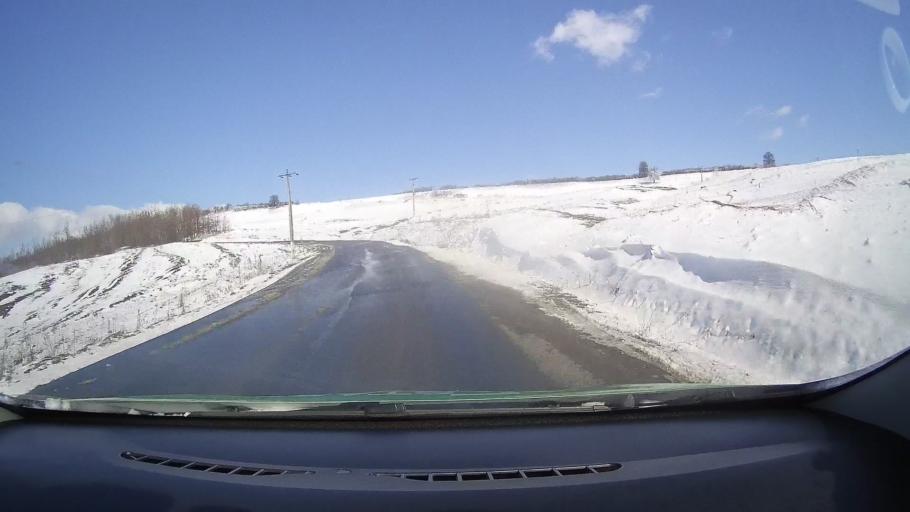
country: RO
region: Sibiu
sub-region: Comuna Rosia
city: Rosia
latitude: 45.8062
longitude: 24.2915
